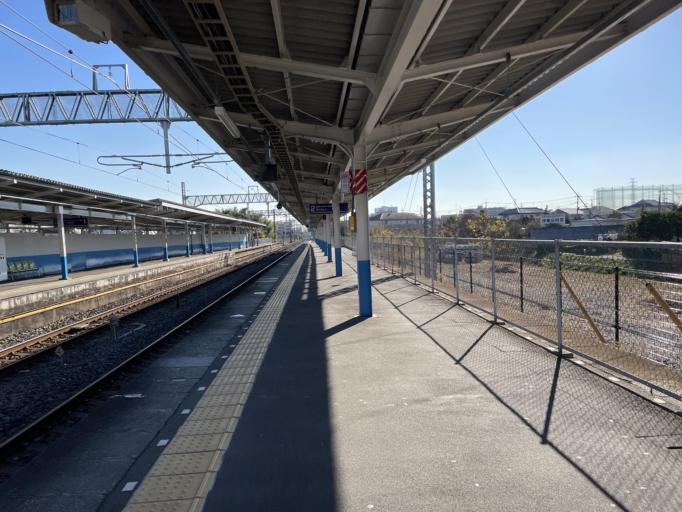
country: JP
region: Saitama
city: Satte
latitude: 36.0742
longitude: 139.7149
